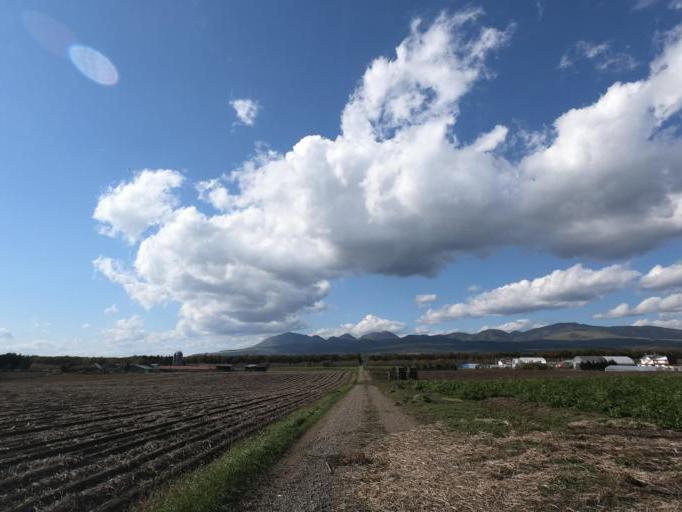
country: JP
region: Hokkaido
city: Otofuke
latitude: 43.2357
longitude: 143.2592
